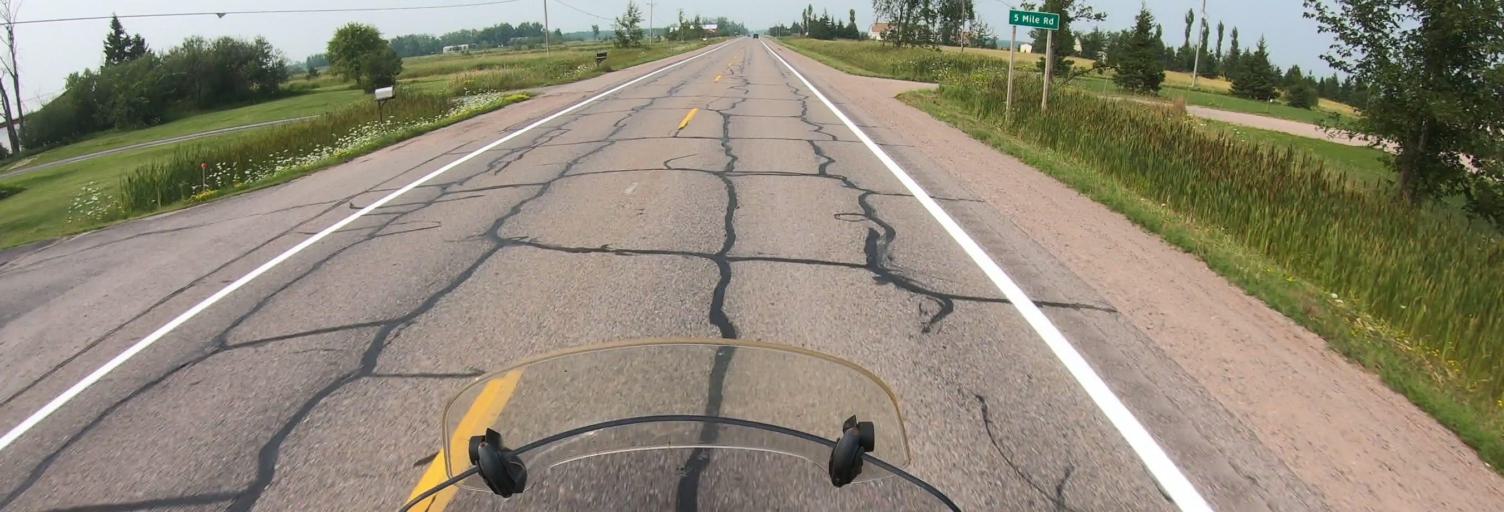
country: US
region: Michigan
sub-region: Chippewa County
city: Sault Ste. Marie
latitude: 46.4317
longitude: -84.3535
